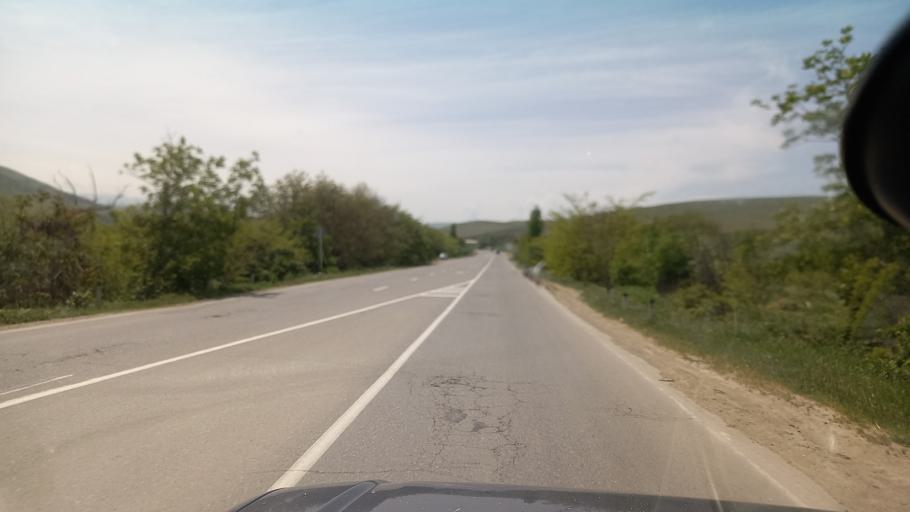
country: RU
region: Dagestan
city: Manas
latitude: 42.7109
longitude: 47.6440
